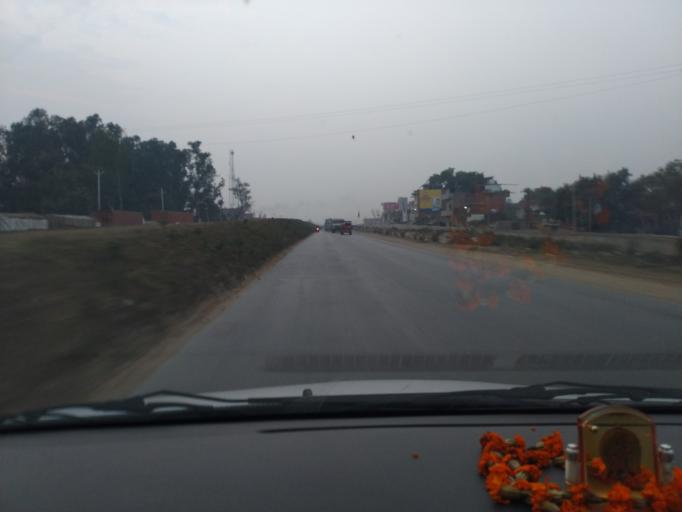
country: IN
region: Uttar Pradesh
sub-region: Chandauli District
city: Chandauli
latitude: 25.2274
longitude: 83.4728
